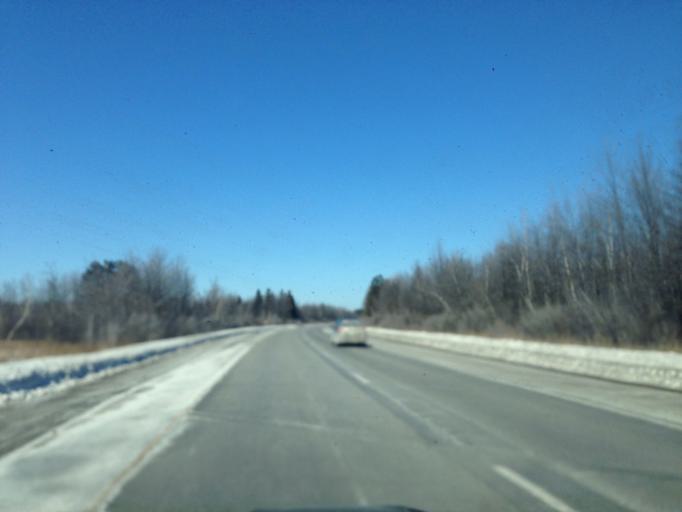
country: CA
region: Ontario
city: Ottawa
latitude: 45.3521
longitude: -75.4600
